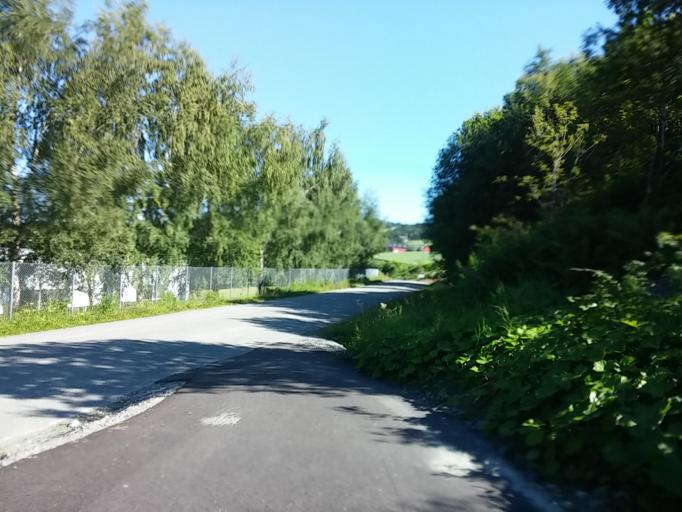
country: NO
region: Sor-Trondelag
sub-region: Malvik
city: Malvik
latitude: 63.4321
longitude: 10.7142
